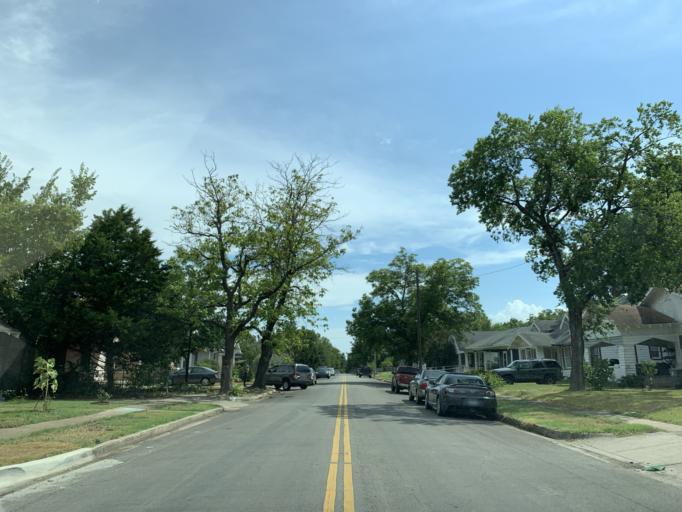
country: US
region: Texas
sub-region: Dallas County
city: Cockrell Hill
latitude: 32.7410
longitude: -96.8405
